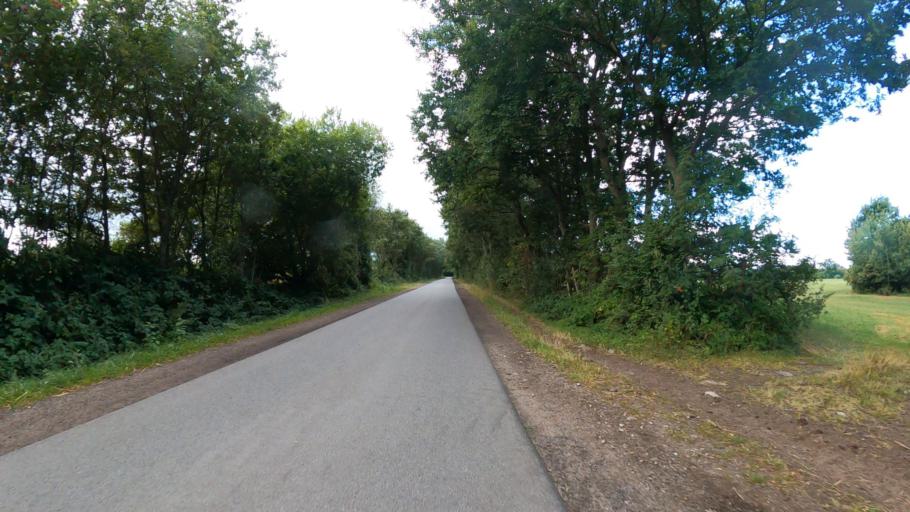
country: DE
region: Schleswig-Holstein
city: Padenstedt
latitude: 54.0273
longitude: 9.9176
